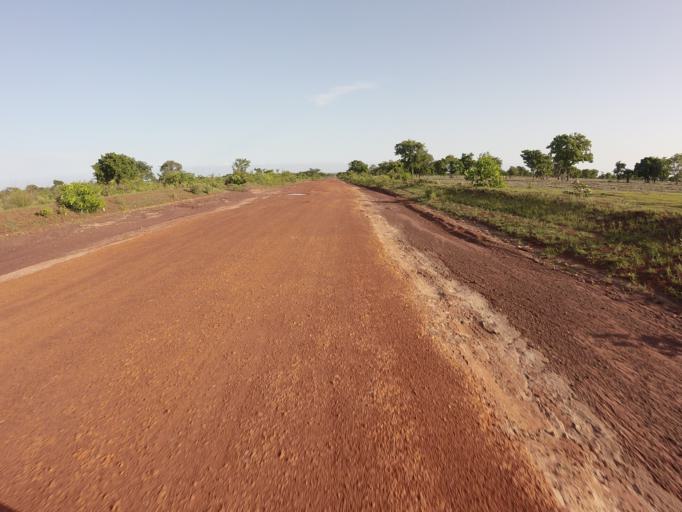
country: TG
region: Savanes
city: Sansanne-Mango
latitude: 10.3800
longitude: -0.0947
